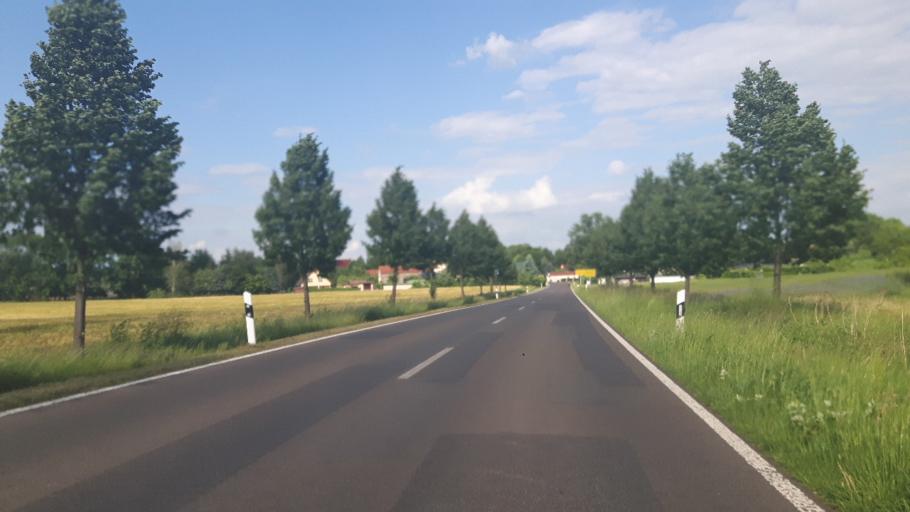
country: DE
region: Brandenburg
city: Melchow
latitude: 52.7110
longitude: 13.7167
